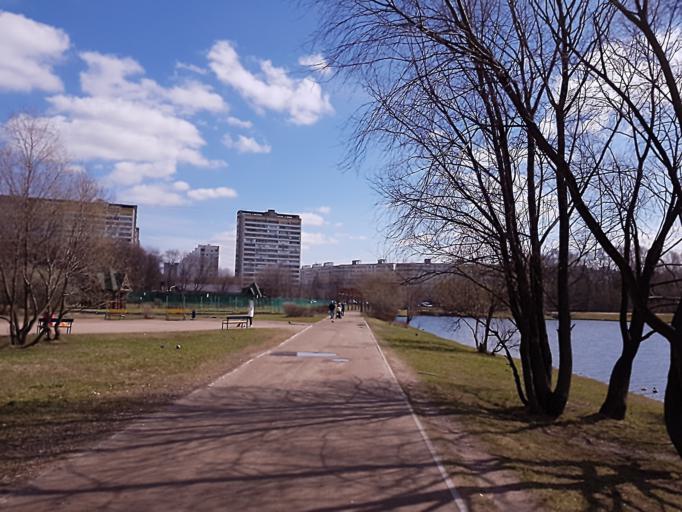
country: RU
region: Moskovskaya
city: Novogireyevo
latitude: 55.7663
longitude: 37.8189
